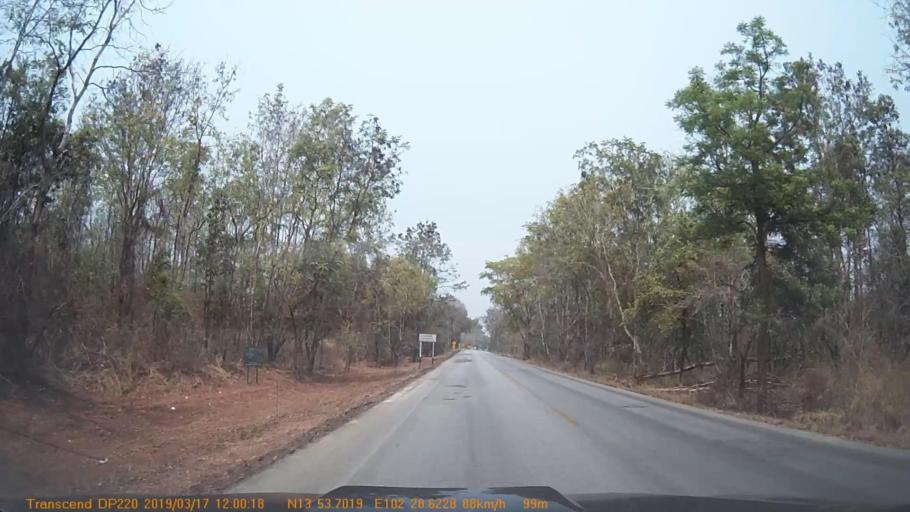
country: TH
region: Sa Kaeo
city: Khok Sung
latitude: 13.8954
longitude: 102.4768
